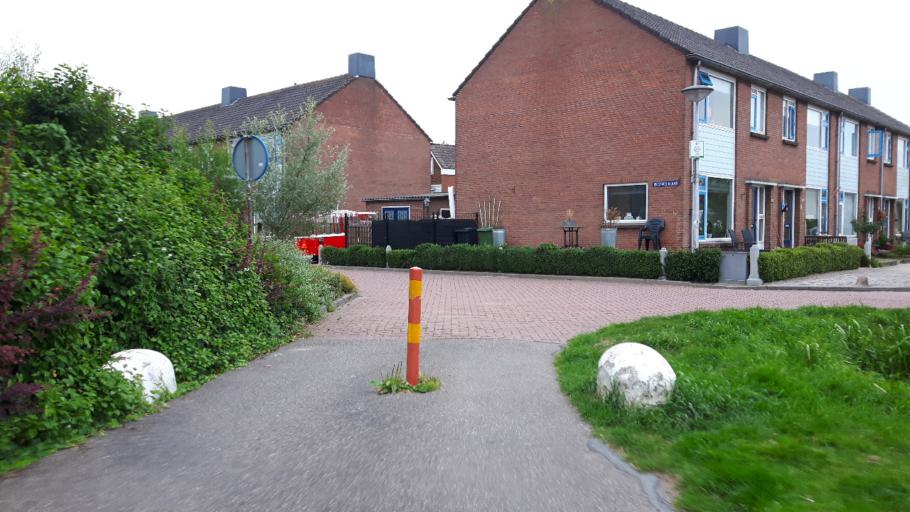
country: NL
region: South Holland
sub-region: Gemeente Kaag en Braassem
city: Oude Wetering
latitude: 52.1904
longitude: 4.6291
